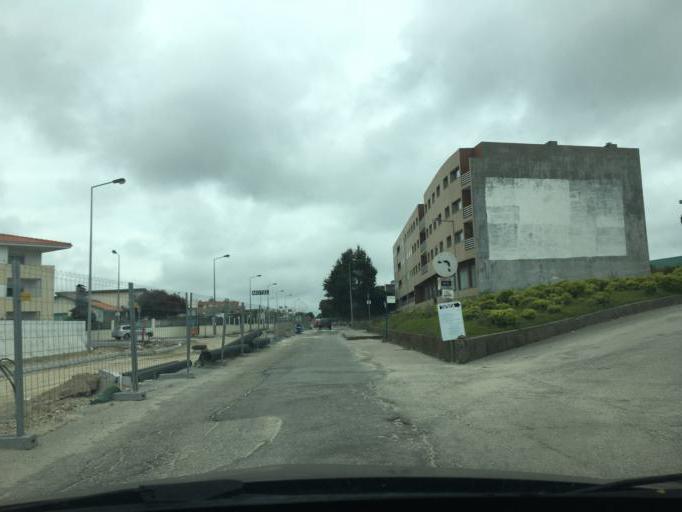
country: PT
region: Porto
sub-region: Matosinhos
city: Santa Cruz do Bispo
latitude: 41.2219
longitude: -8.6858
